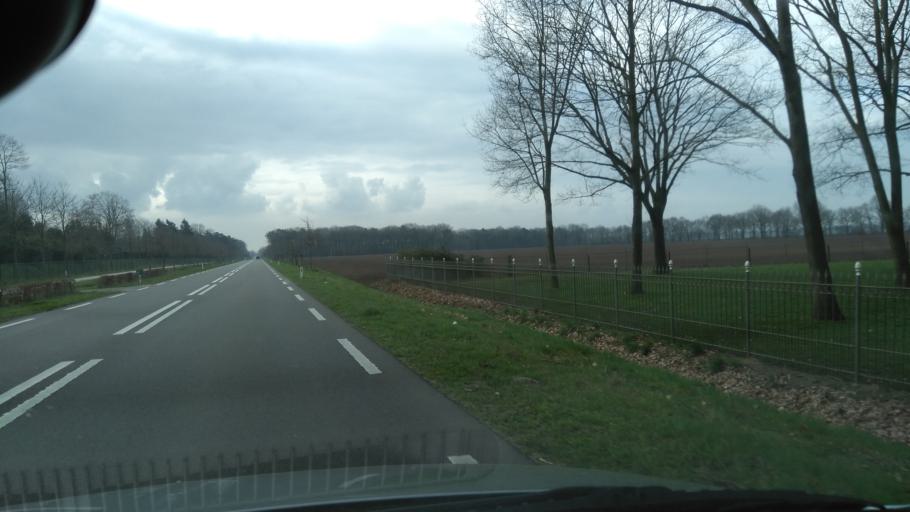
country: NL
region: North Brabant
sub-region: Gemeente Baarle-Nassau
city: Baarle-Nassau
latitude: 51.4211
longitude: 4.9340
